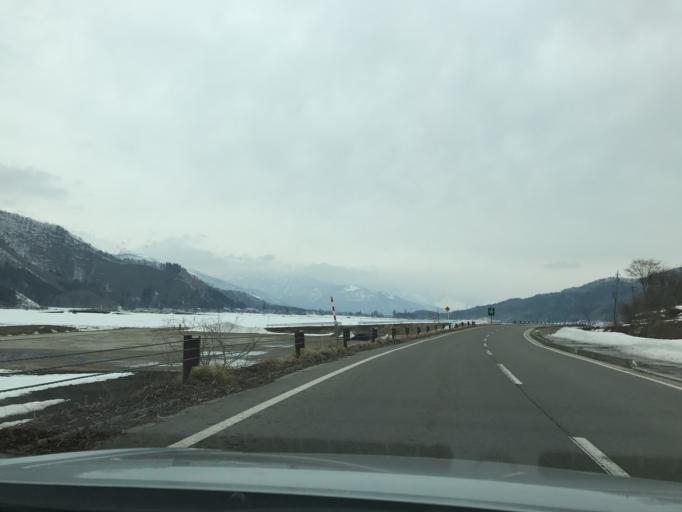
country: JP
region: Nagano
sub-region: Kitaazumi Gun
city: Hakuba
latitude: 36.6401
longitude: 137.8522
